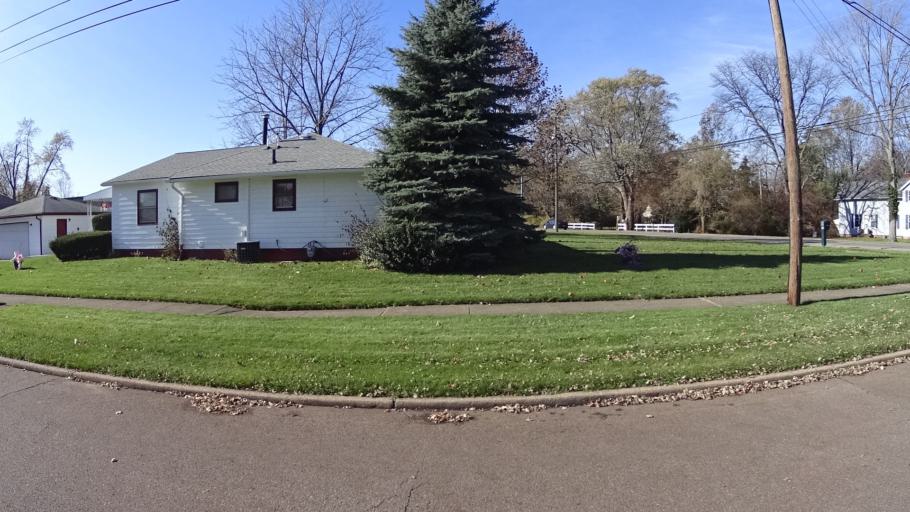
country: US
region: Ohio
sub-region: Lorain County
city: Sheffield Lake
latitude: 41.4989
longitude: -82.0710
